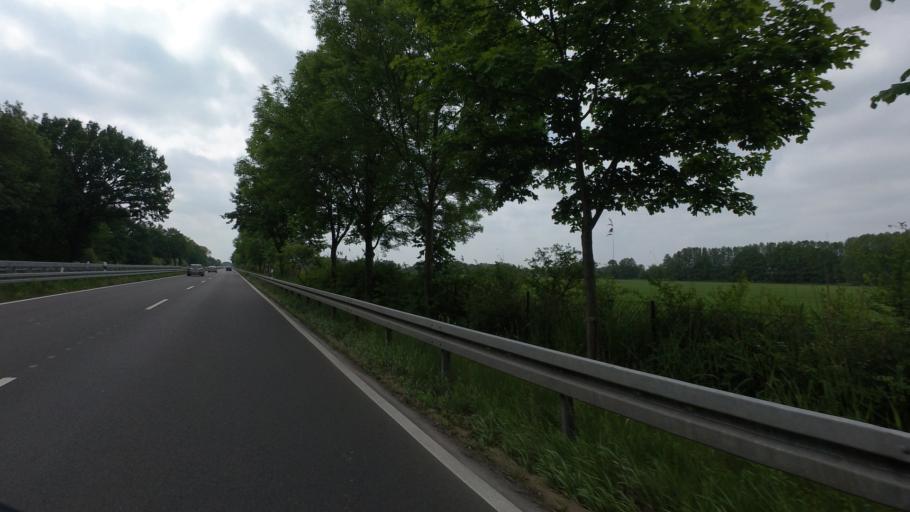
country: DE
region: Brandenburg
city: Peitz
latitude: 51.8316
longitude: 14.3871
